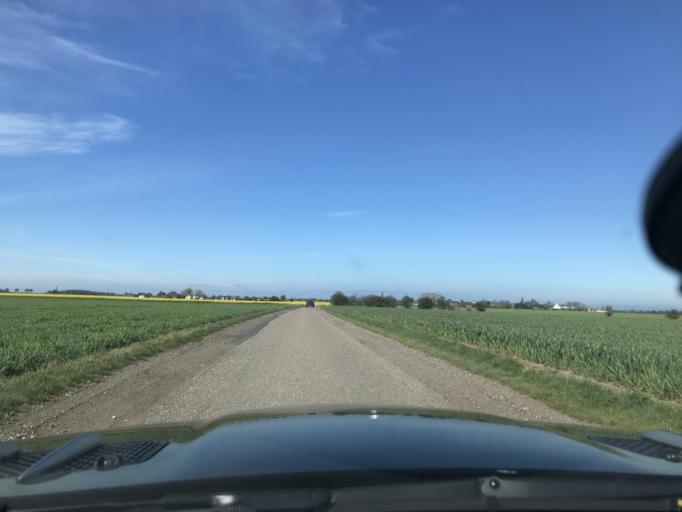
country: DE
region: Schleswig-Holstein
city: Grossenbrode
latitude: 54.4572
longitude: 11.0607
